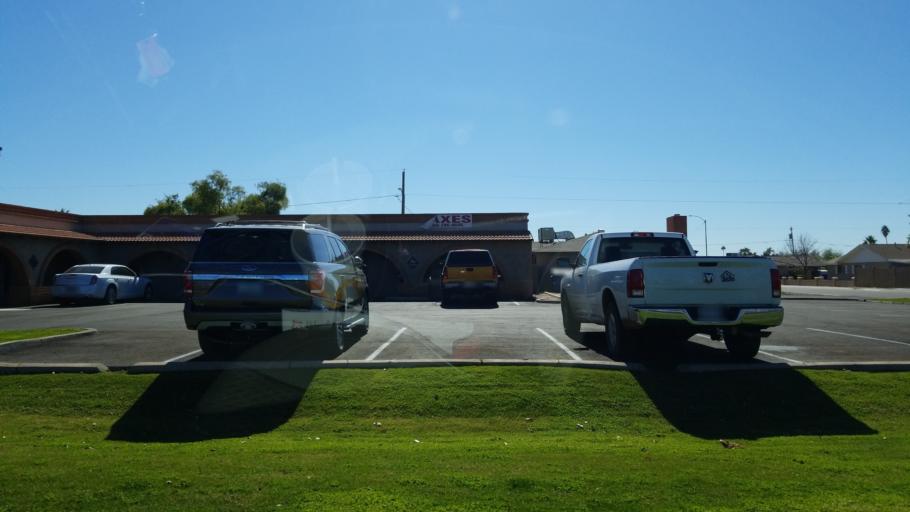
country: US
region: Arizona
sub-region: Maricopa County
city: Chandler
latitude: 33.3206
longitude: -111.8481
